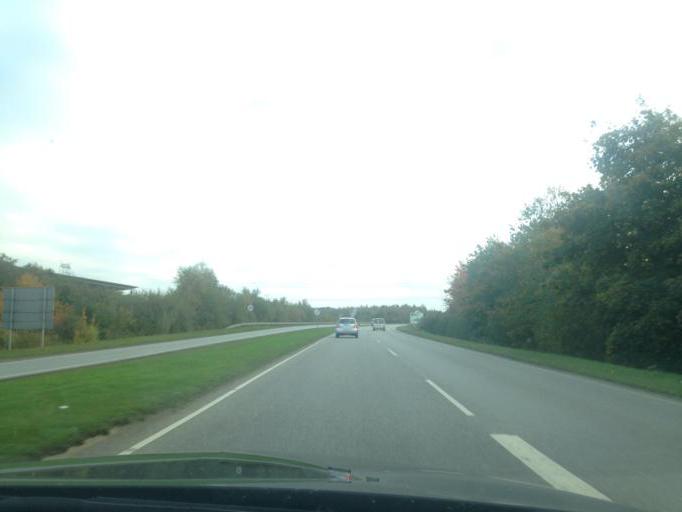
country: DK
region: South Denmark
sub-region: Kolding Kommune
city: Kolding
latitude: 55.5365
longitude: 9.4899
